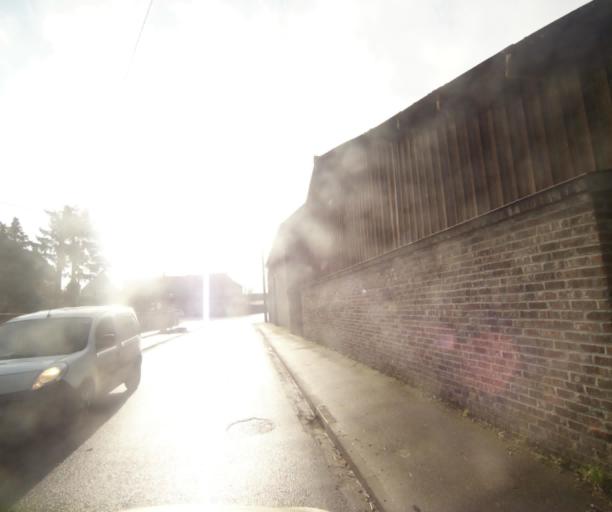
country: FR
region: Nord-Pas-de-Calais
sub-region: Departement du Nord
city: Thiant
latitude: 50.2875
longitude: 3.4555
